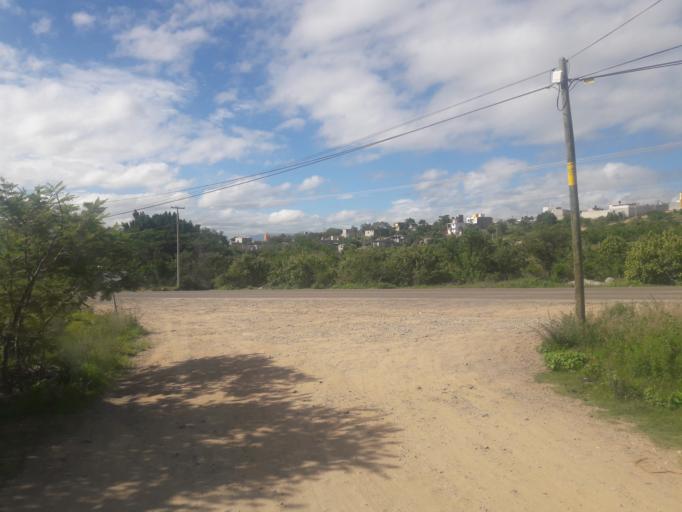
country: MX
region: Oaxaca
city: Ciudad de Huajuapam de Leon
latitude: 17.8335
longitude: -97.7854
